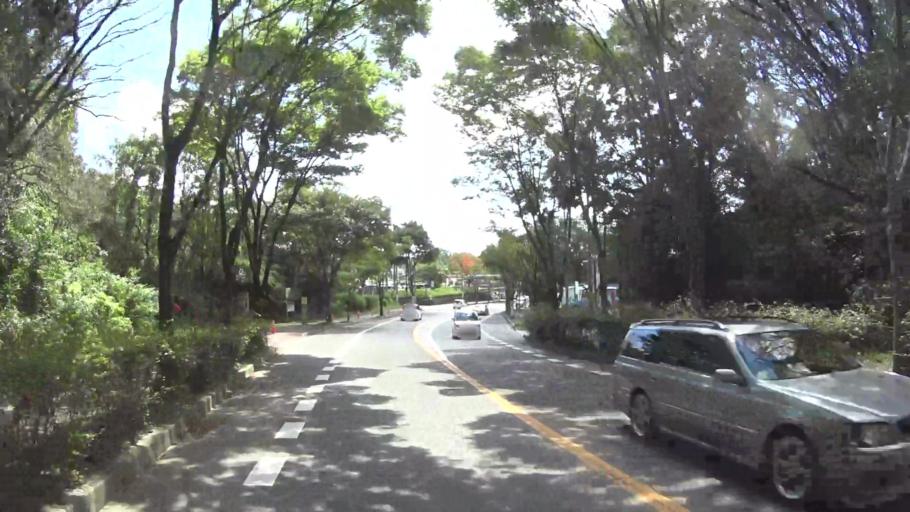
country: JP
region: Kyoto
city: Uji
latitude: 34.8576
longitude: 135.8009
